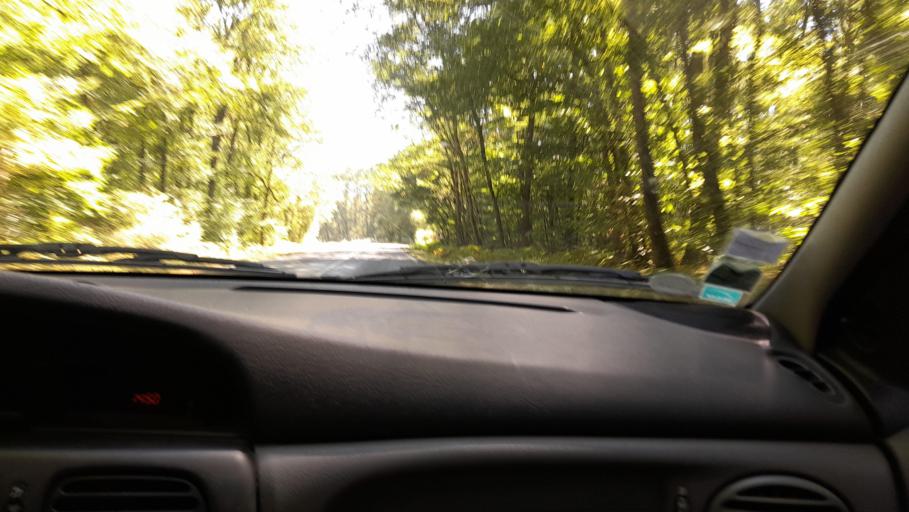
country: FR
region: Pays de la Loire
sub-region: Departement de Maine-et-Loire
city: Pouance
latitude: 47.6886
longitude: -1.1851
